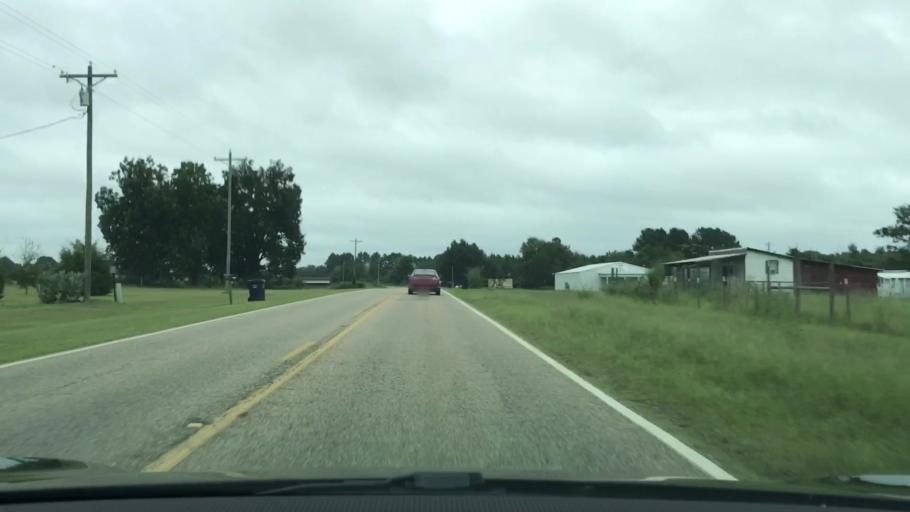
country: US
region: Alabama
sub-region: Geneva County
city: Samson
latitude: 31.1788
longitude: -86.1457
